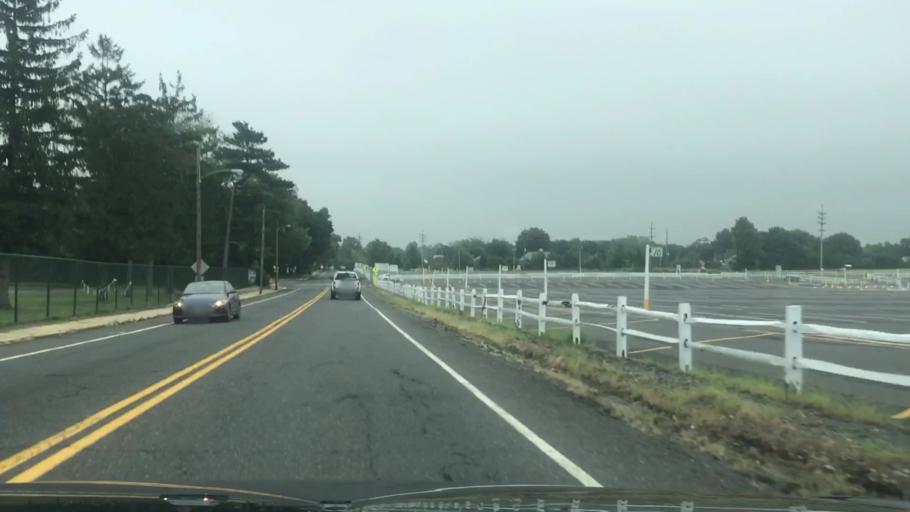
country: US
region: New Jersey
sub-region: Monmouth County
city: Oceanport
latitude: 40.3086
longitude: -74.0211
